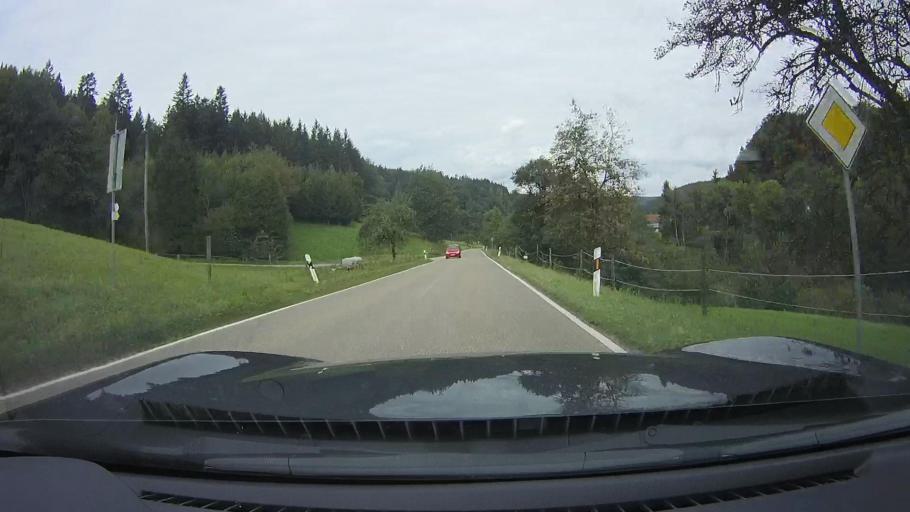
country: DE
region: Baden-Wuerttemberg
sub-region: Regierungsbezirk Stuttgart
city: Kaisersbach
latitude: 48.9529
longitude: 9.6376
